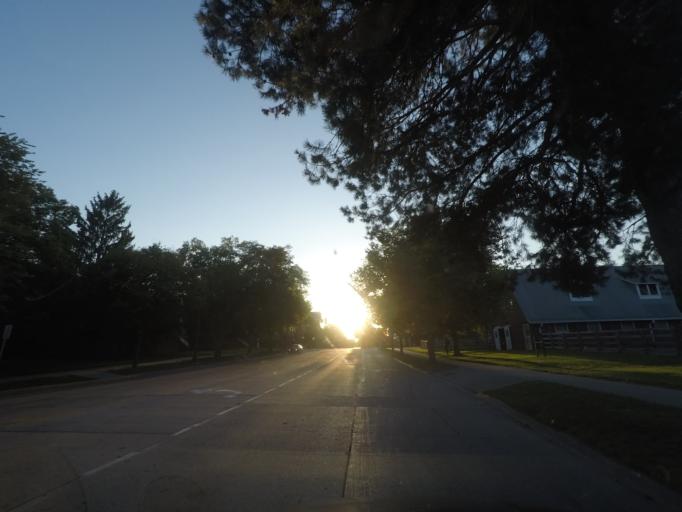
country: US
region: Iowa
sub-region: Story County
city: Ames
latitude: 42.0306
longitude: -93.6435
